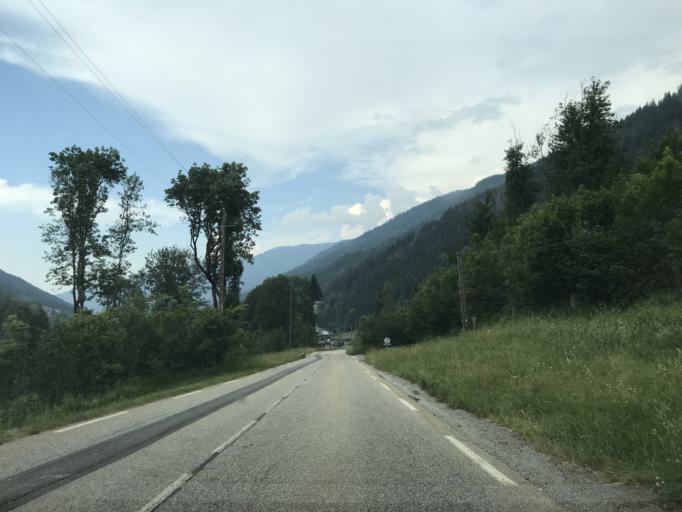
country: FR
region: Rhone-Alpes
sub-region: Departement de l'Isere
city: Allevard
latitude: 45.3138
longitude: 6.0832
